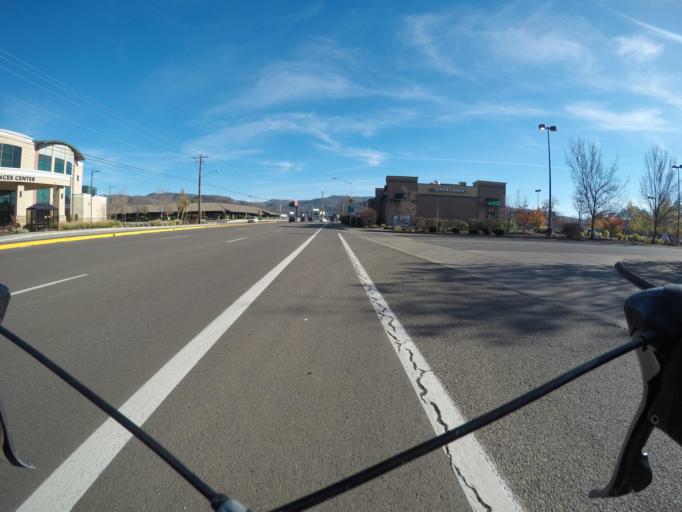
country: US
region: Oregon
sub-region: Douglas County
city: Roseburg
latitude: 43.2402
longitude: -123.3638
